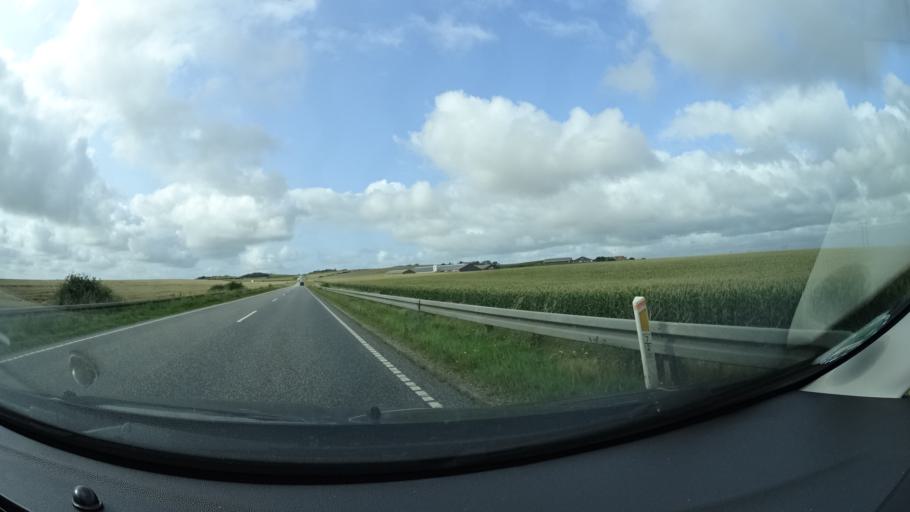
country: DK
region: Central Jutland
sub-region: Lemvig Kommune
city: Harboore
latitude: 56.5709
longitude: 8.2153
